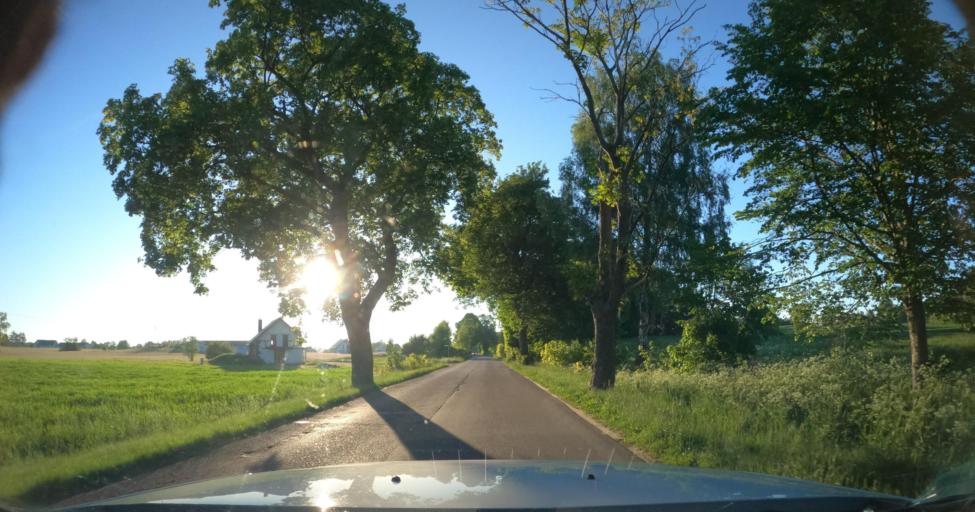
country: PL
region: Pomeranian Voivodeship
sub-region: Powiat kartuski
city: Suleczyno
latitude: 54.3328
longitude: 17.7707
